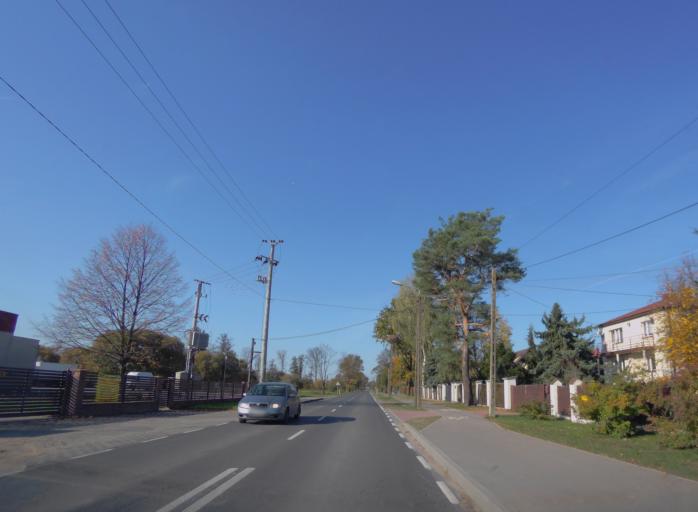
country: PL
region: Masovian Voivodeship
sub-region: Powiat minski
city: Halinow
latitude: 52.1894
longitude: 21.3329
